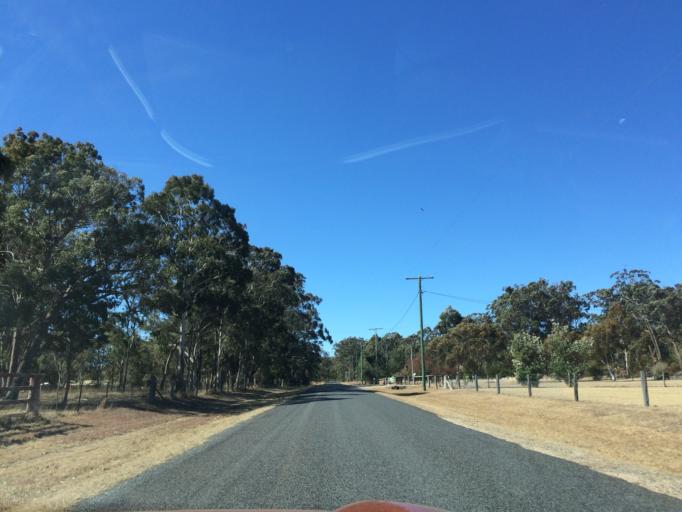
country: AU
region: Queensland
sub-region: Southern Downs
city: Stanthorpe
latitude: -28.6941
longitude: 152.0192
